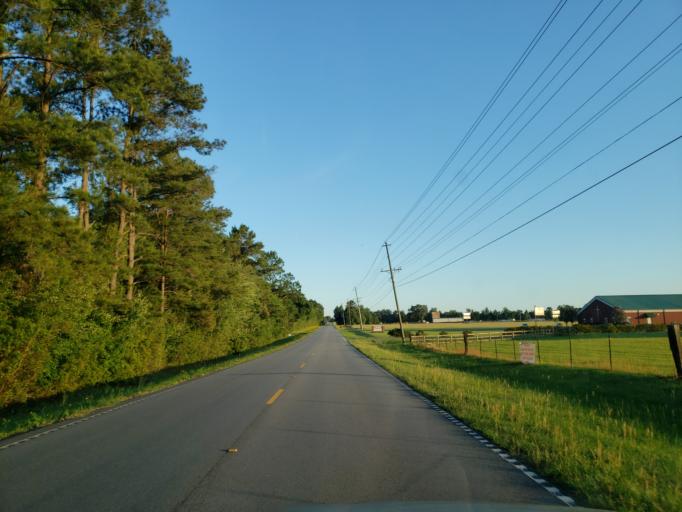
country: US
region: Georgia
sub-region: Lowndes County
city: Valdosta
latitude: 30.7029
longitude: -83.2409
